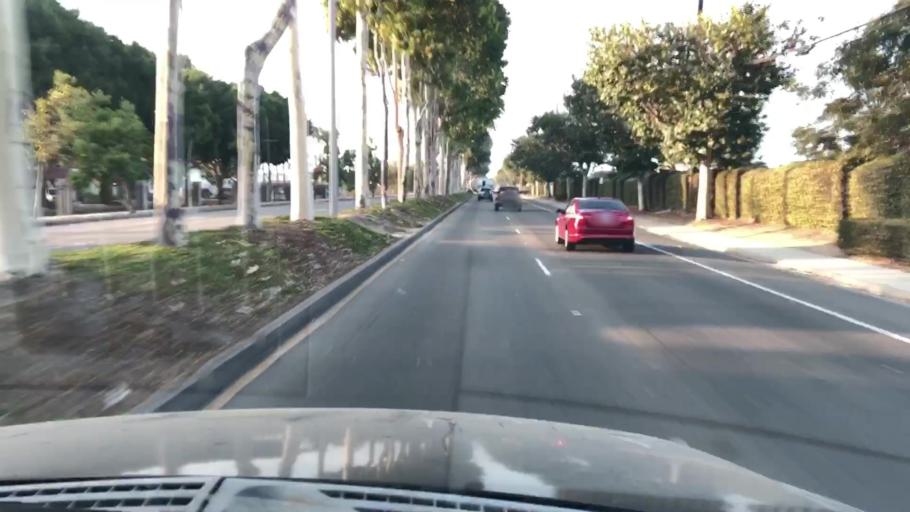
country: US
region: California
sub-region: Ventura County
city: Port Hueneme
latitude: 34.1638
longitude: -119.1951
